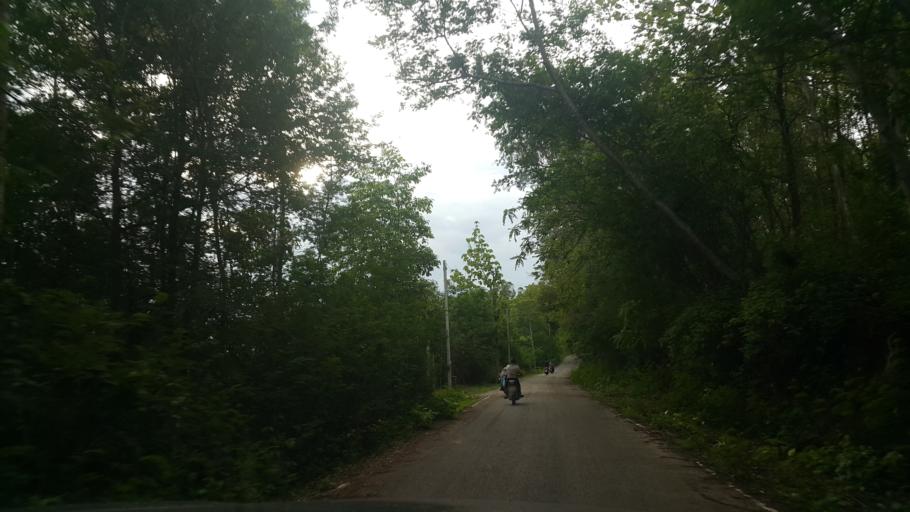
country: TH
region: Chiang Mai
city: Mae On
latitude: 18.7243
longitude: 99.2319
